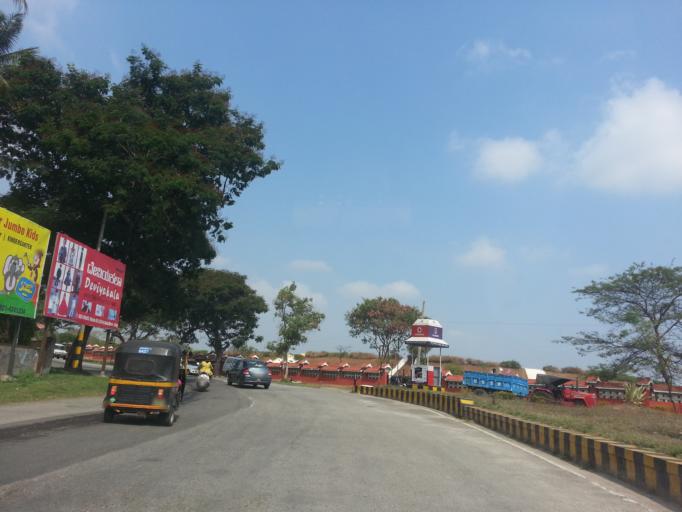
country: IN
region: Karnataka
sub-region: Mysore
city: Mysore
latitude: 12.3322
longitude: 76.6560
